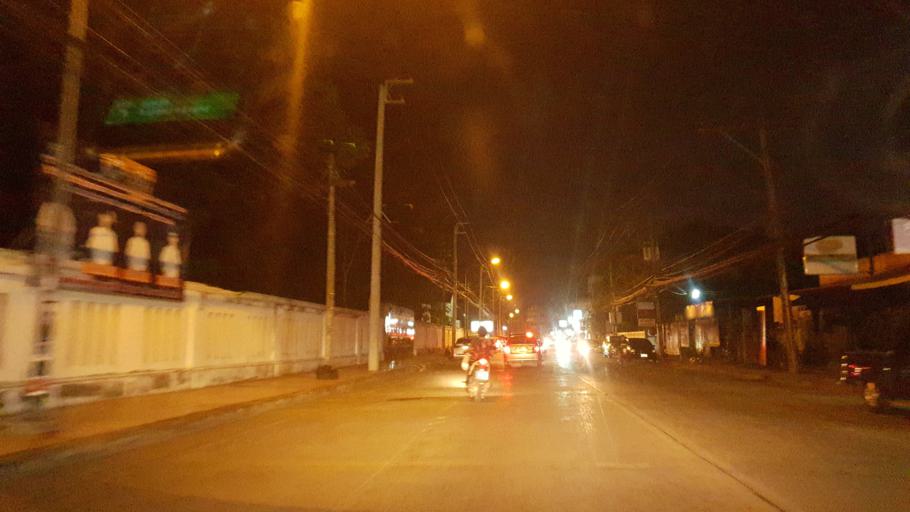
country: TH
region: Phitsanulok
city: Phitsanulok
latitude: 16.8094
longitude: 100.2700
